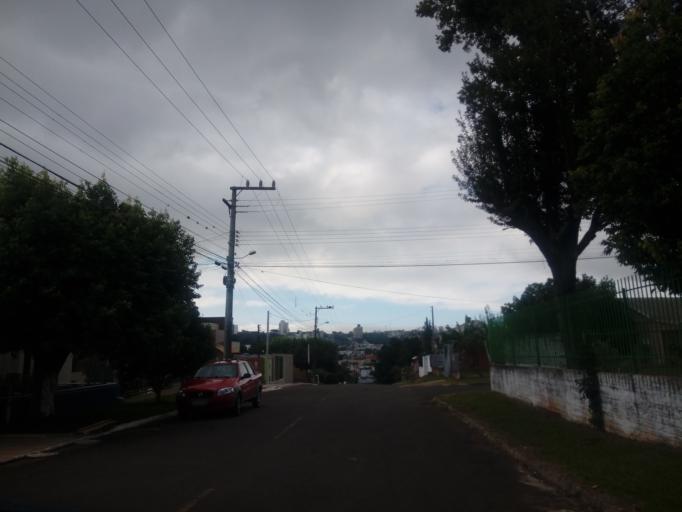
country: BR
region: Santa Catarina
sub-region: Chapeco
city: Chapeco
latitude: -27.1159
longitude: -52.6230
